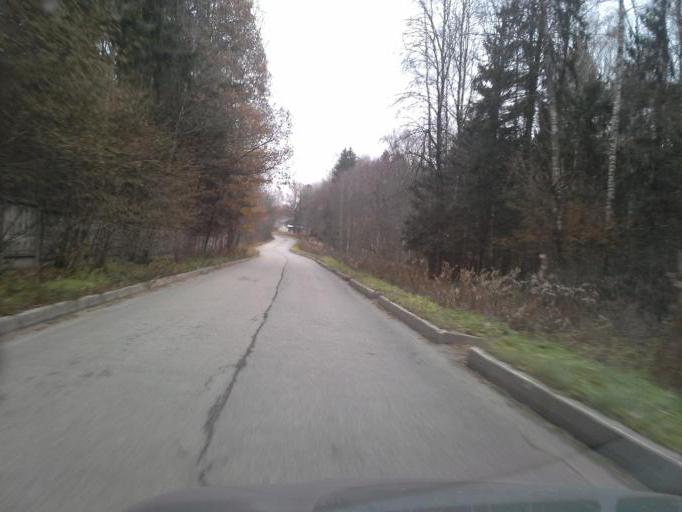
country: RU
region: Moskovskaya
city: Peshki
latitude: 56.1474
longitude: 37.0468
